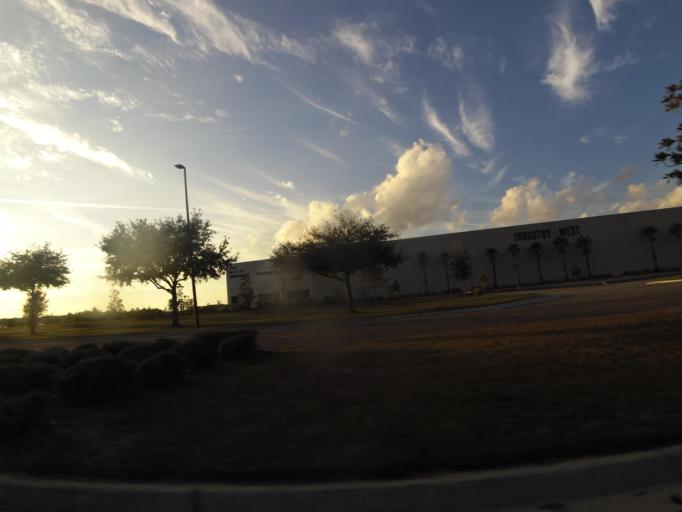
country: US
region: Florida
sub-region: Duval County
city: Baldwin
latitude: 30.2722
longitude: -81.8854
